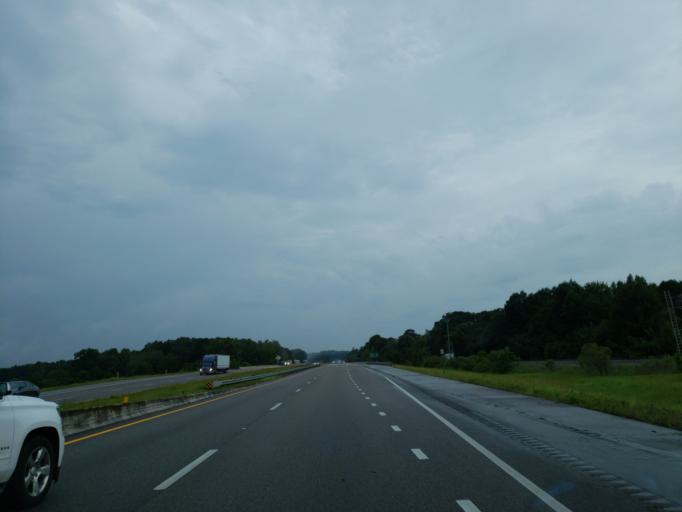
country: US
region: Mississippi
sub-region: Lauderdale County
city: Marion
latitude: 32.3814
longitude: -88.6374
